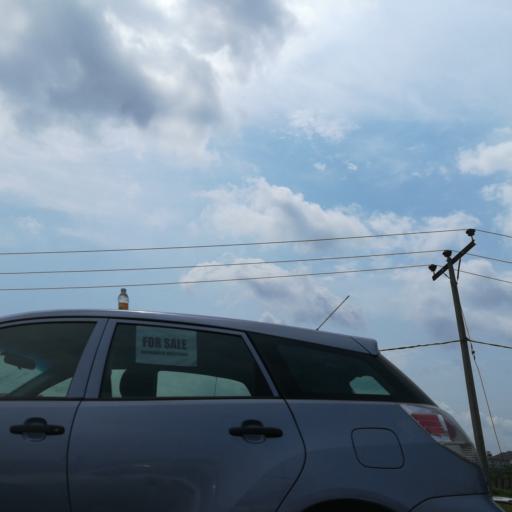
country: NG
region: Rivers
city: Port Harcourt
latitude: 4.8899
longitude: 7.0111
